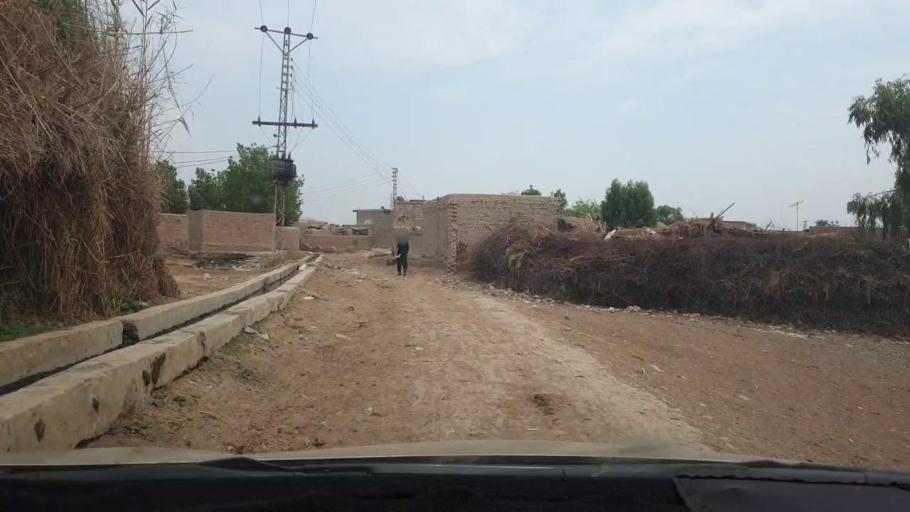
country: PK
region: Sindh
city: Ratodero
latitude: 27.7669
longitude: 68.3339
